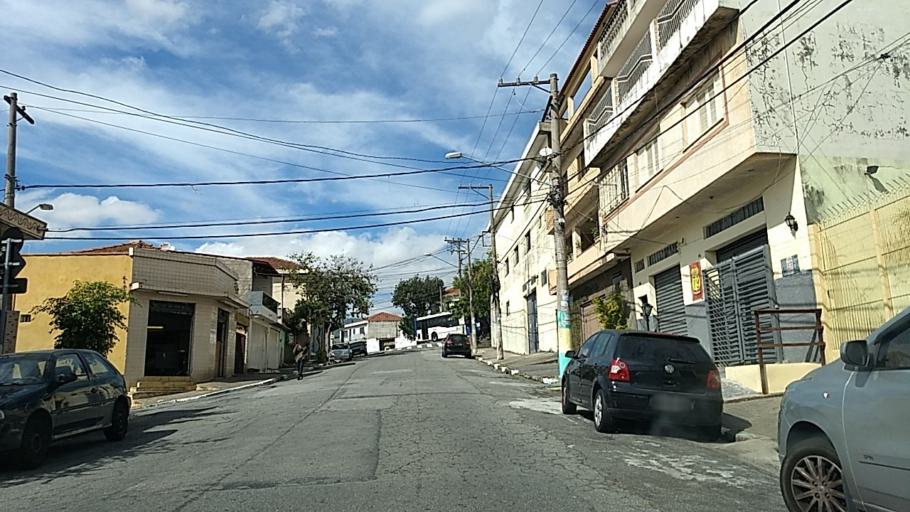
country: BR
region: Sao Paulo
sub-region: Guarulhos
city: Guarulhos
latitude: -23.4948
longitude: -46.5785
